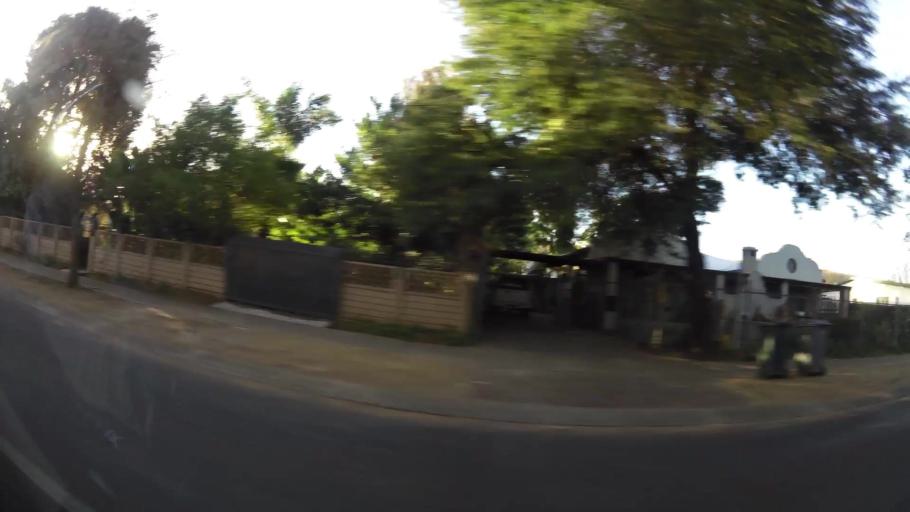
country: ZA
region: Gauteng
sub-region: City of Tshwane Metropolitan Municipality
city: Pretoria
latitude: -25.7010
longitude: 28.2381
